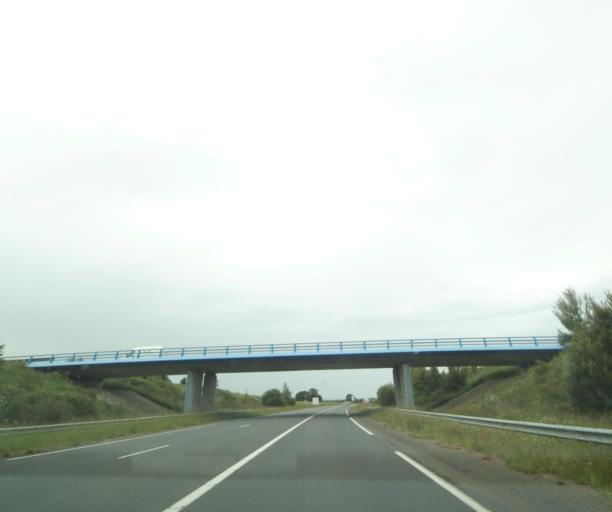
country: FR
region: Poitou-Charentes
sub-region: Departement des Deux-Sevres
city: Saint-Pardoux
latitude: 46.5453
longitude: -0.3126
